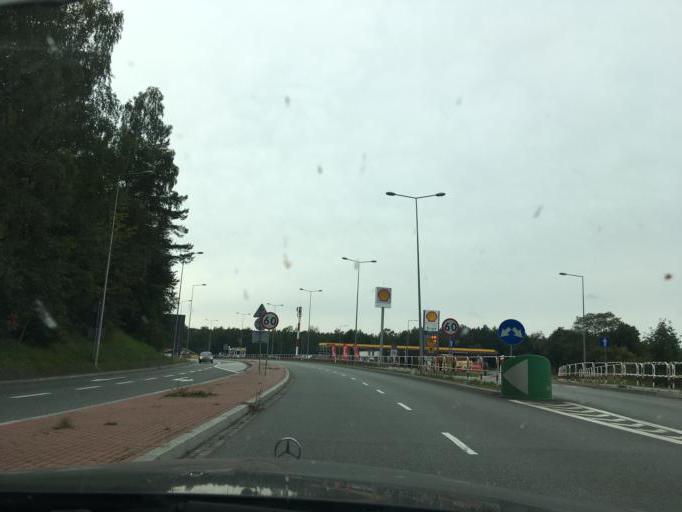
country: CZ
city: Velke Porici
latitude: 50.4334
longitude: 16.2019
